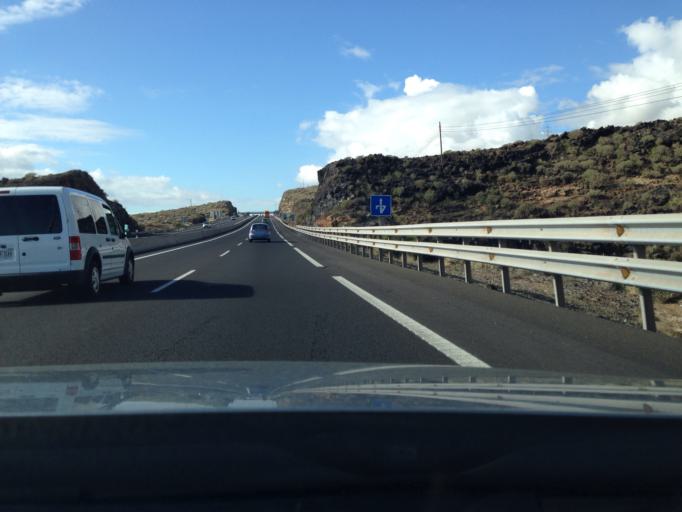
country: ES
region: Canary Islands
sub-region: Provincia de Santa Cruz de Tenerife
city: Fasnia
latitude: 28.2204
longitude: -16.4170
